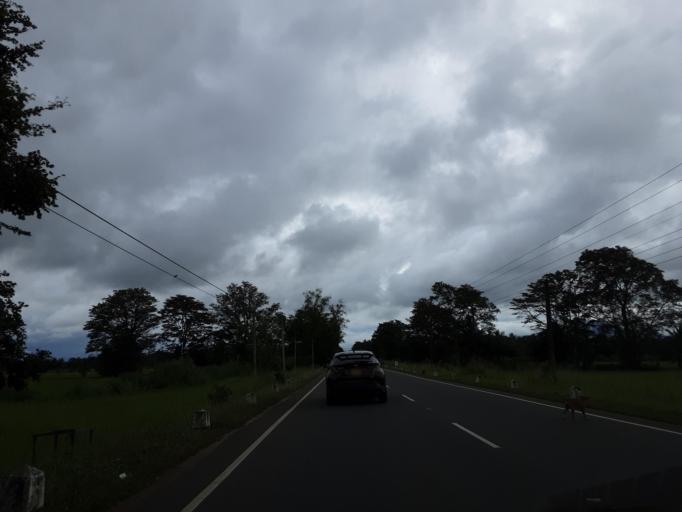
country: LK
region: Uva
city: Badulla
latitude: 7.3719
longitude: 81.0655
